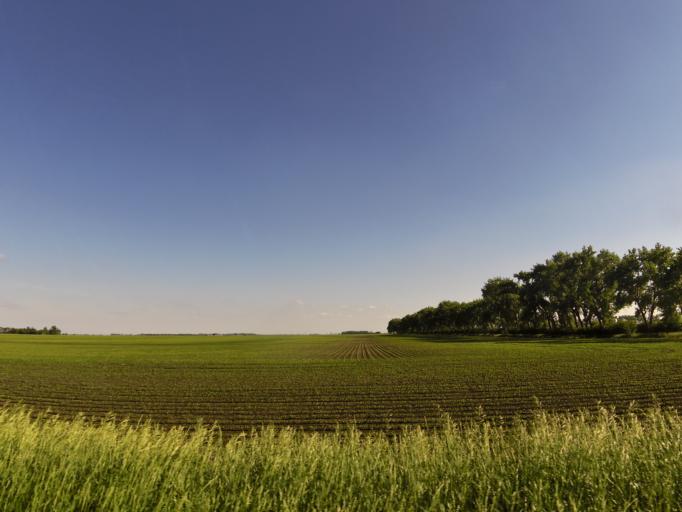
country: US
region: North Dakota
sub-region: Walsh County
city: Grafton
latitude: 48.3975
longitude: -97.2222
